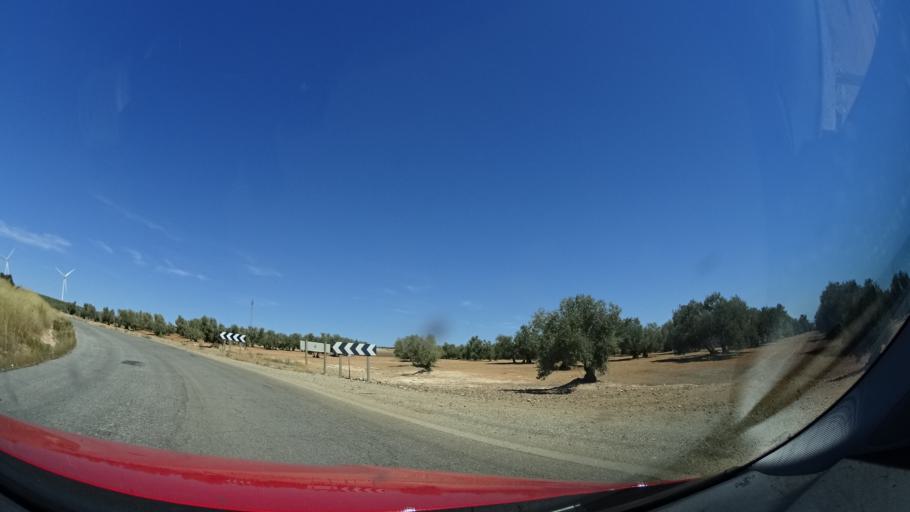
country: ES
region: Andalusia
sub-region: Provincia de Malaga
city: Sierra de Yeguas
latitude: 37.0964
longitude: -4.8672
